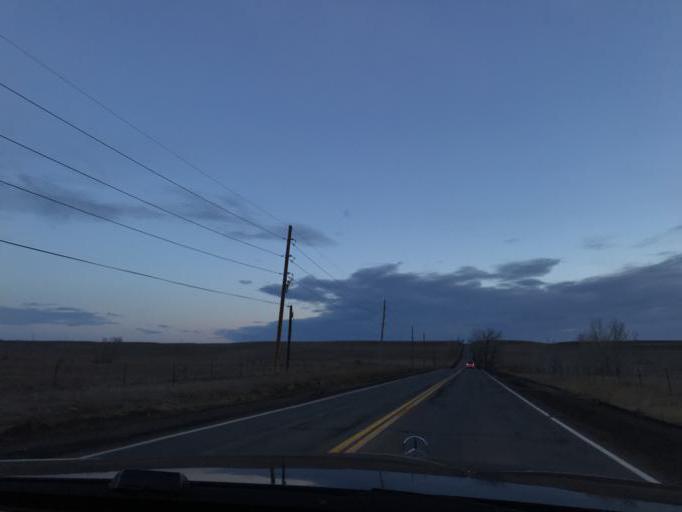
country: US
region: Colorado
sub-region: Boulder County
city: Superior
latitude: 39.8755
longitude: -105.1654
